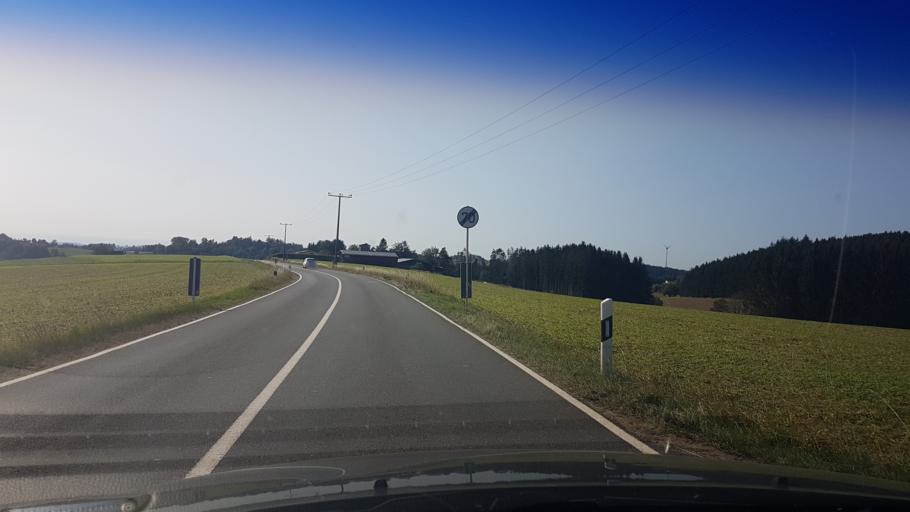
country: DE
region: Bavaria
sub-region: Upper Franconia
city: Marktschorgast
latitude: 50.0959
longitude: 11.6800
